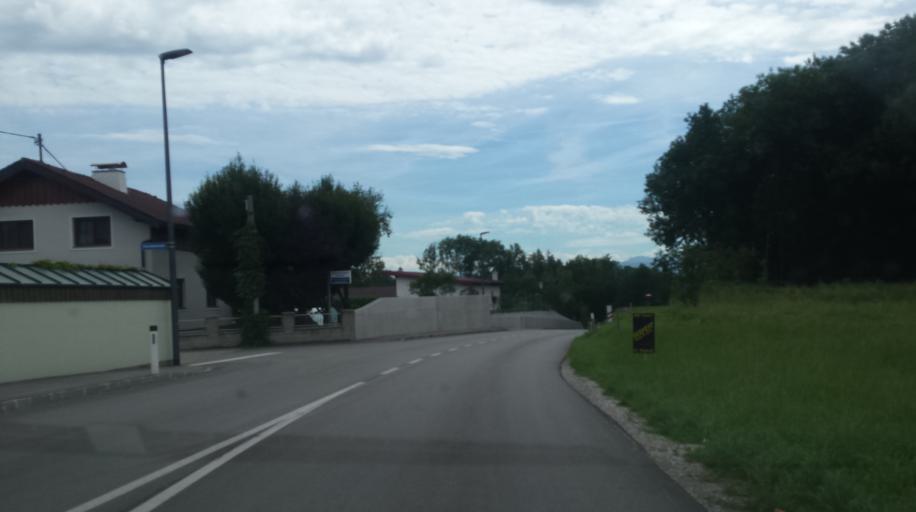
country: AT
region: Upper Austria
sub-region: Wels-Land
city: Bad Wimsbach-Neydharting
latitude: 48.0594
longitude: 13.9058
